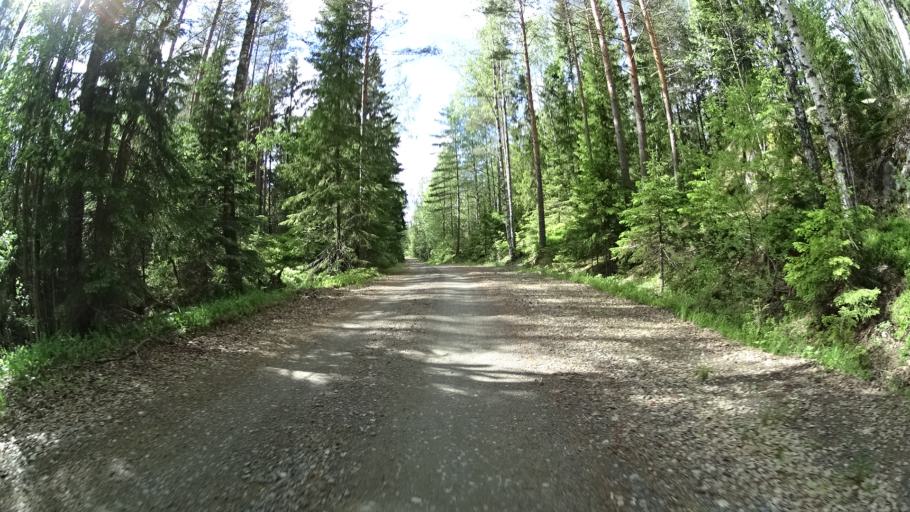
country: FI
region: Varsinais-Suomi
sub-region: Salo
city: Kisko
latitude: 60.1783
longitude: 23.5459
